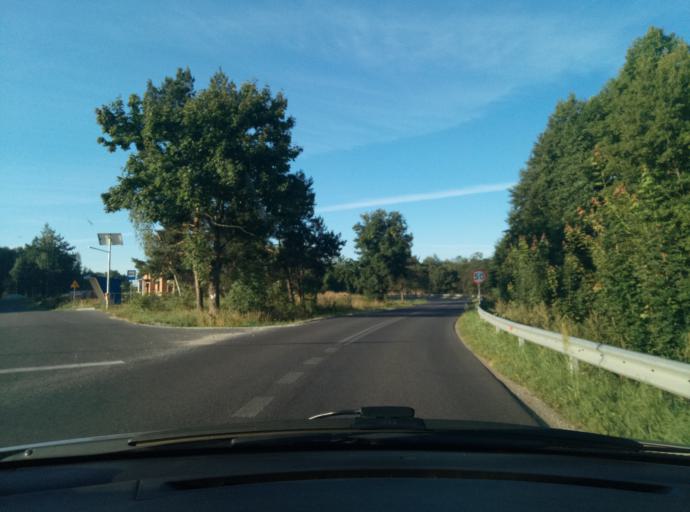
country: PL
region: Kujawsko-Pomorskie
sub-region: Powiat wabrzeski
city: Wabrzezno
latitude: 53.2323
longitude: 18.9535
